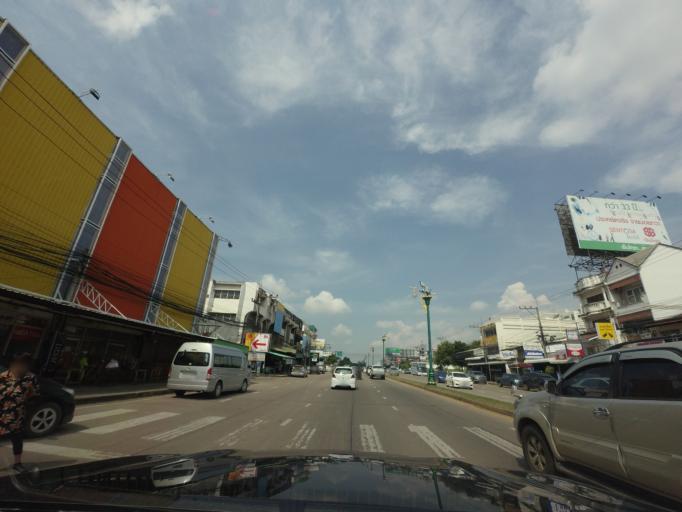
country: TH
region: Khon Kaen
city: Khon Kaen
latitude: 16.4401
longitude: 102.8249
